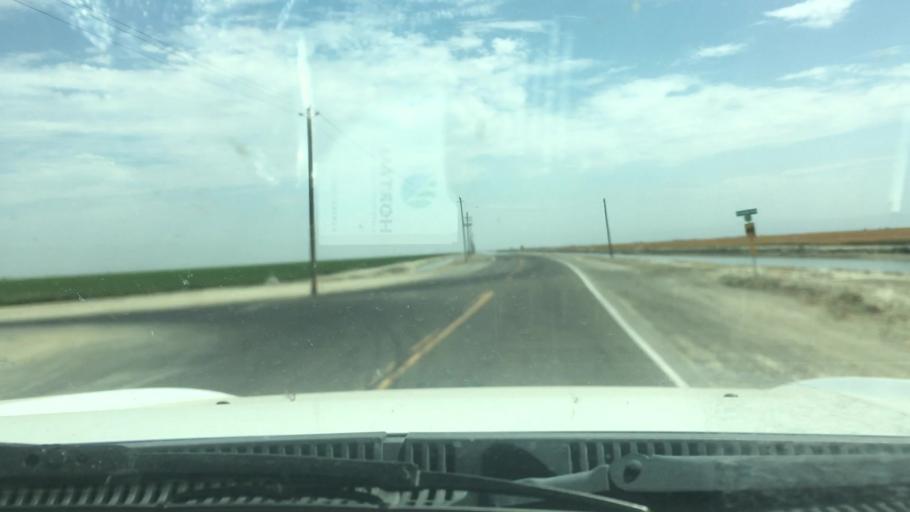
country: US
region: California
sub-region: Tulare County
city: Alpaugh
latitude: 35.8916
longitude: -119.5734
